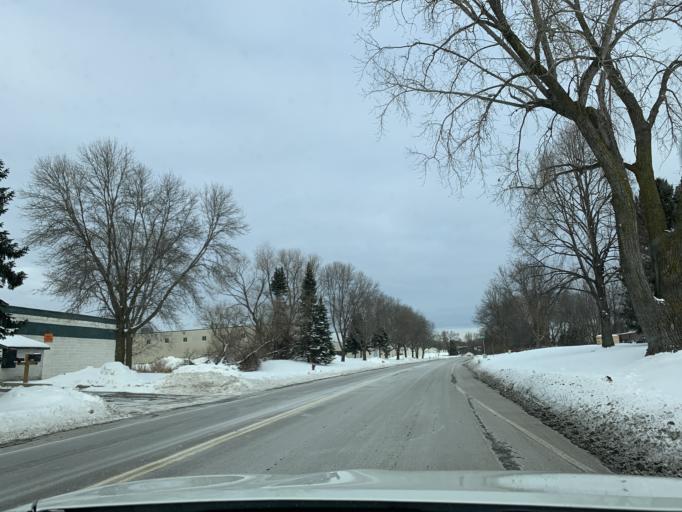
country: US
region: Minnesota
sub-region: Hennepin County
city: West Coon Rapids
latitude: 45.1779
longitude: -93.2979
